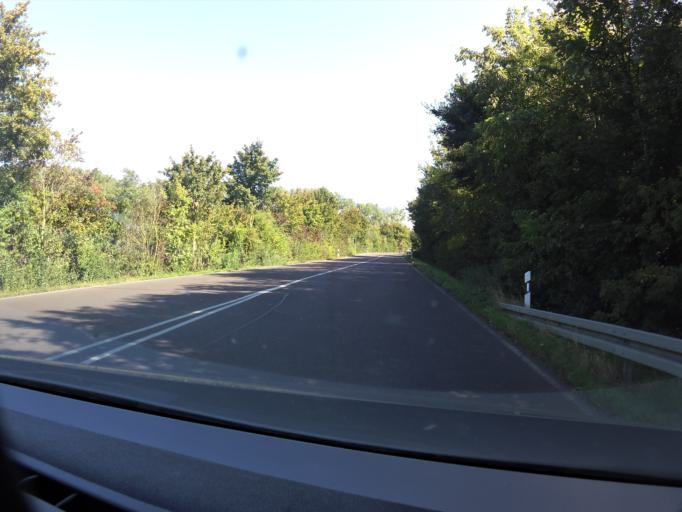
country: DE
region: Saxony-Anhalt
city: Diesdorf
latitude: 52.0759
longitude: 11.5668
